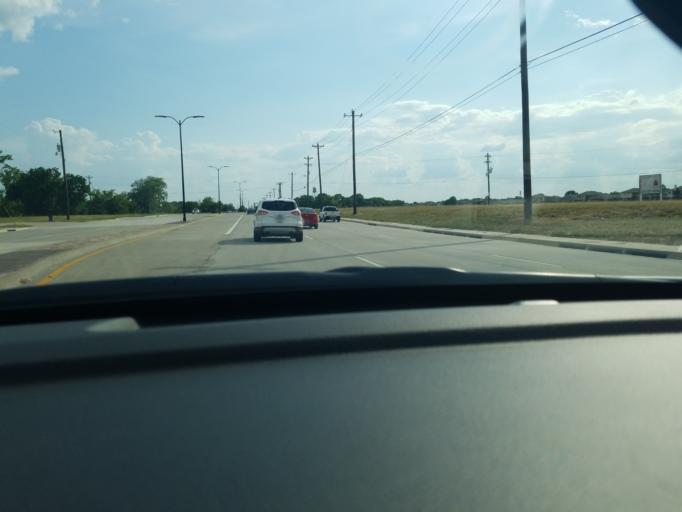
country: US
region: Texas
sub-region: Denton County
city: Little Elm
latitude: 33.1680
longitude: -96.9263
